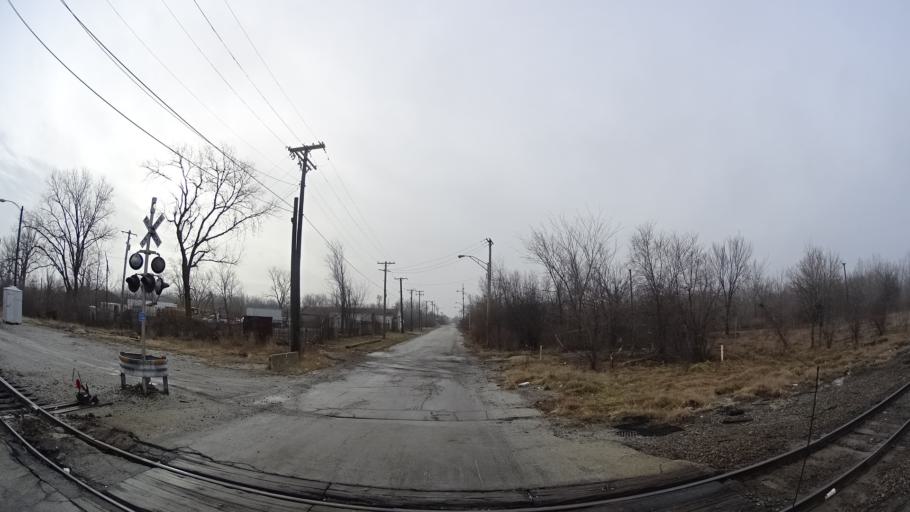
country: US
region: Illinois
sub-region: Cook County
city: Chicago Heights
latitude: 41.5008
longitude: -87.6210
